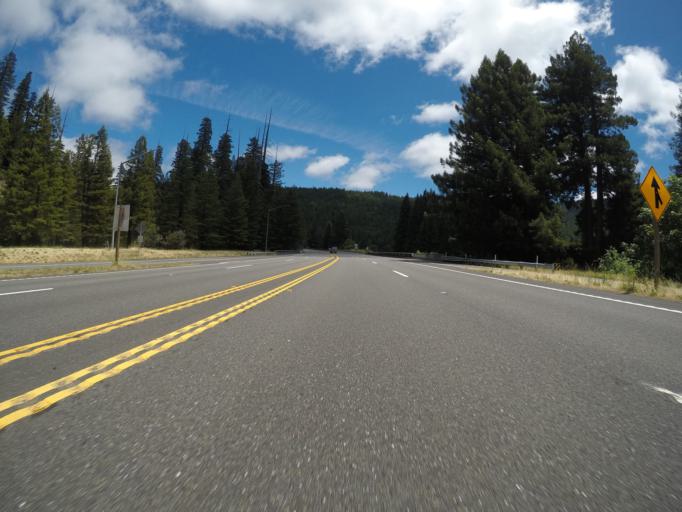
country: US
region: California
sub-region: Humboldt County
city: Redway
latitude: 40.2667
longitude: -123.8712
